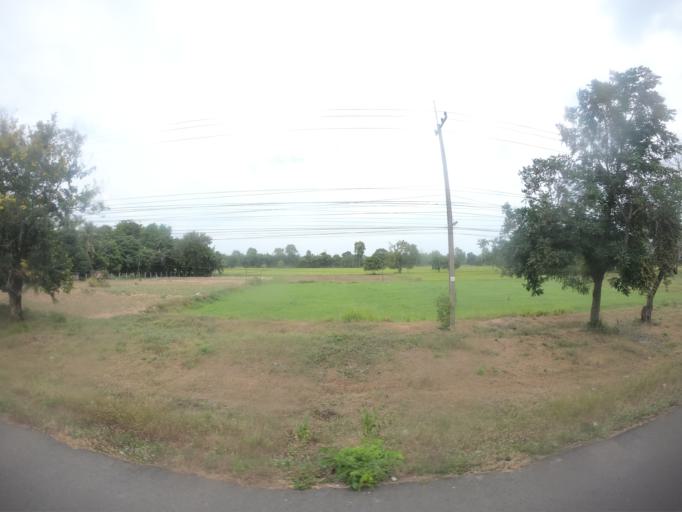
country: TH
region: Kalasin
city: Khong Chai
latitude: 16.1419
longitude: 103.4255
